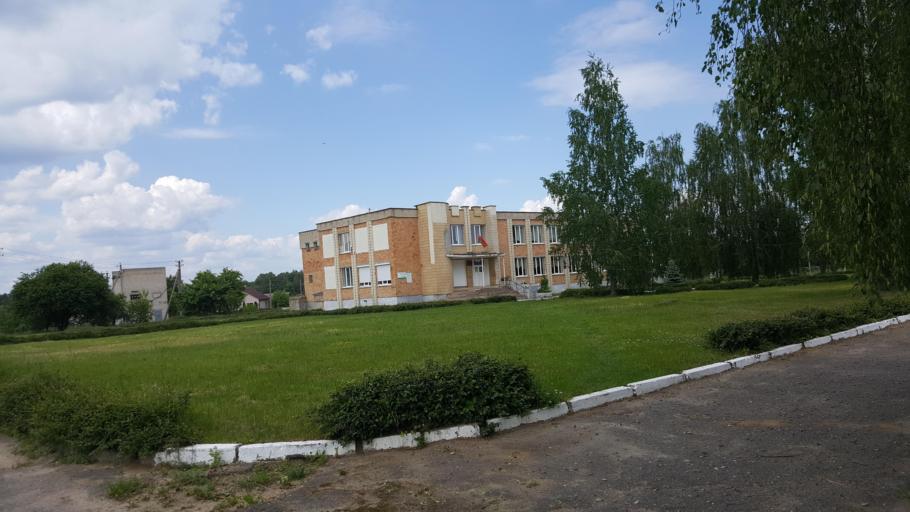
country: PL
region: Podlasie
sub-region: Powiat hajnowski
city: Bialowieza
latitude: 52.6717
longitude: 24.0859
